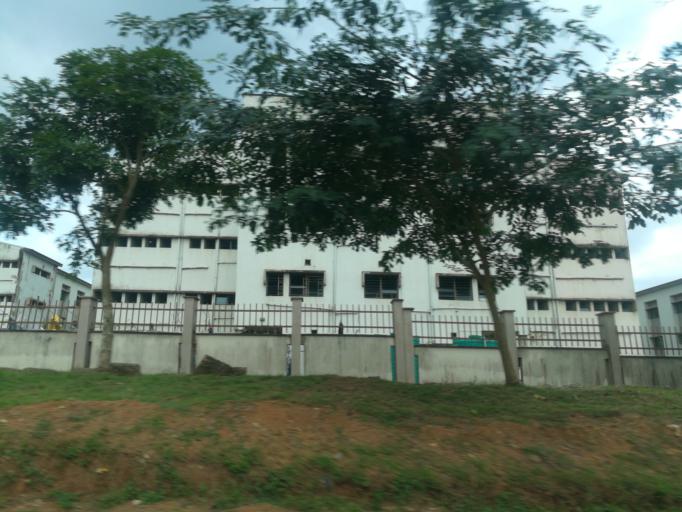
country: NG
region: Oyo
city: Ibadan
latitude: 7.4394
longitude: 3.8940
